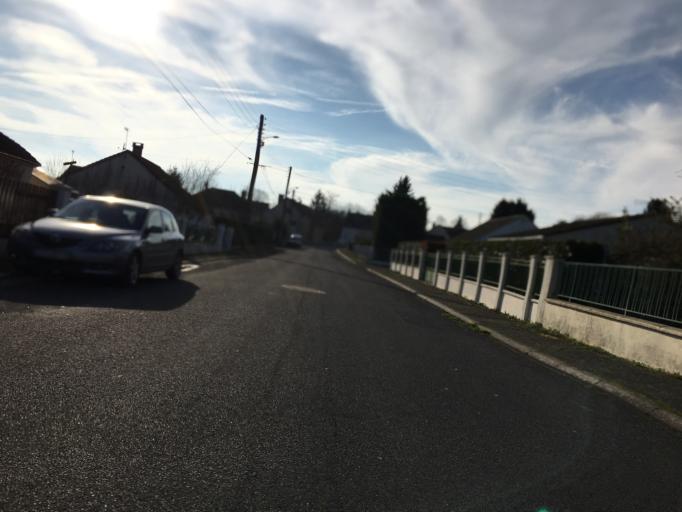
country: FR
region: Centre
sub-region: Departement du Loiret
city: Tavers
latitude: 47.7919
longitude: 1.5298
